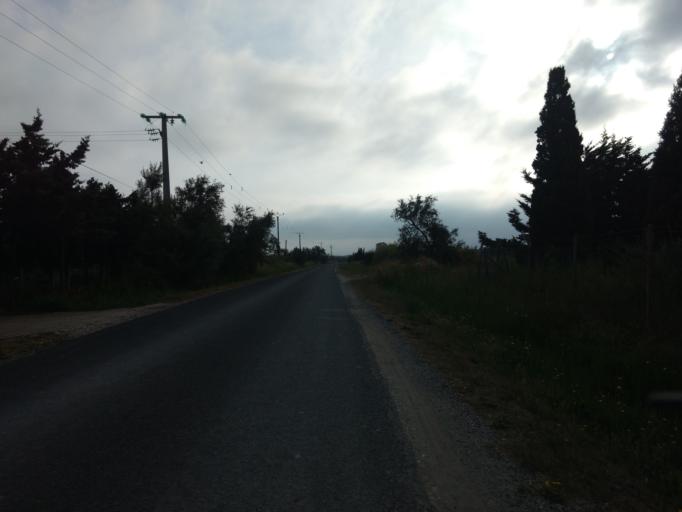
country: FR
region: Languedoc-Roussillon
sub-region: Departement des Pyrenees-Orientales
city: Le Barcares
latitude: 42.7866
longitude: 3.0193
